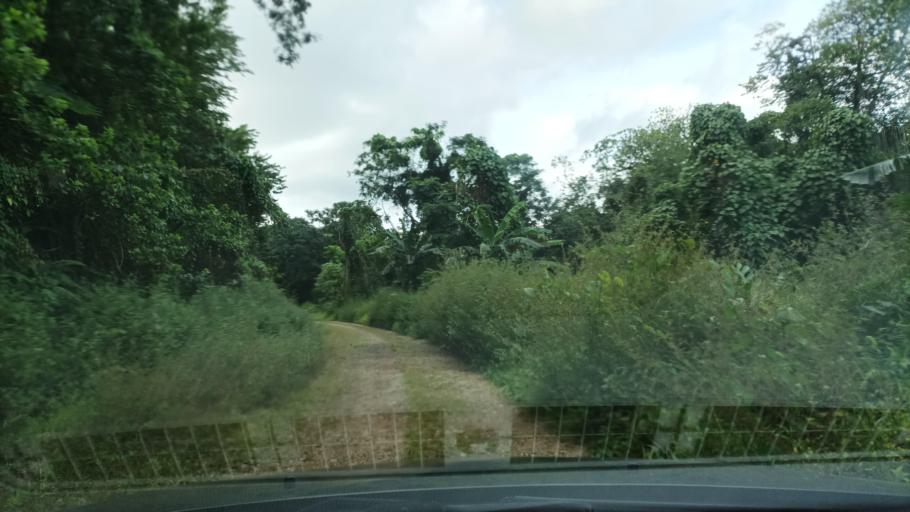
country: FM
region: Kosrae
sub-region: Utwe Municipality
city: Utwe
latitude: 5.2756
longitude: 162.9541
